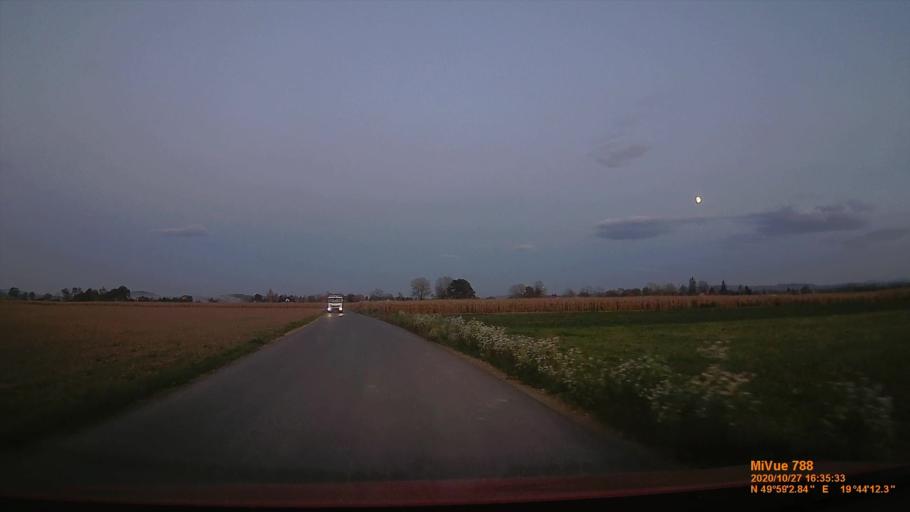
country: PL
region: Lesser Poland Voivodeship
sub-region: Powiat krakowski
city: Wolowice
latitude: 49.9843
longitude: 19.7373
